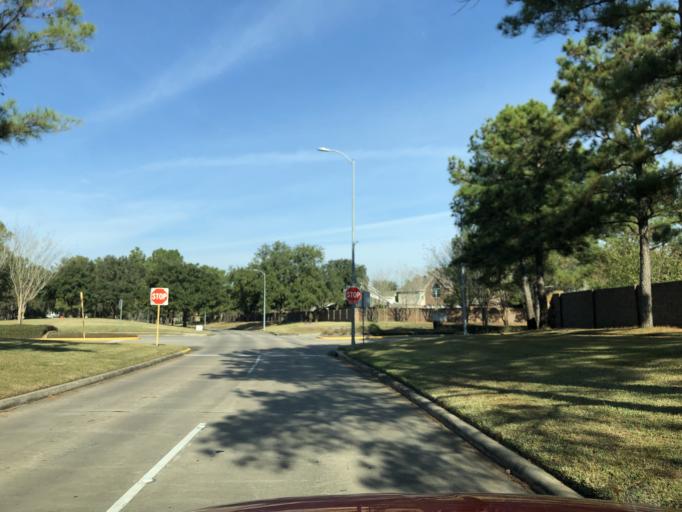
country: US
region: Texas
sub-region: Harris County
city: Tomball
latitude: 30.0287
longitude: -95.5642
